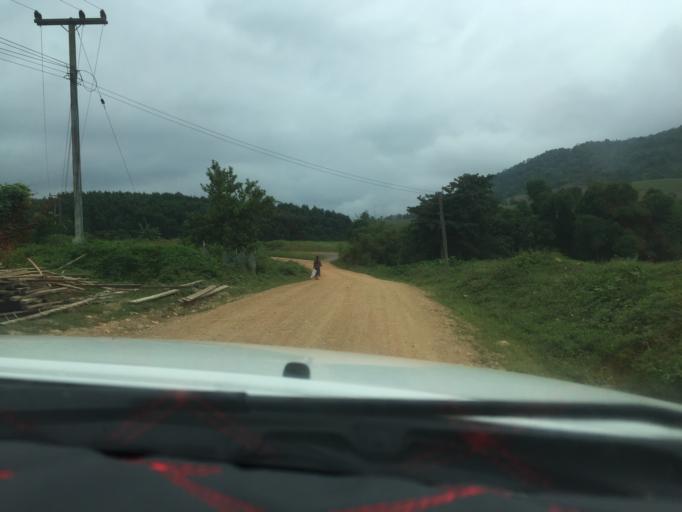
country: TH
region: Phayao
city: Phu Sang
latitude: 19.6934
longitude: 100.5013
